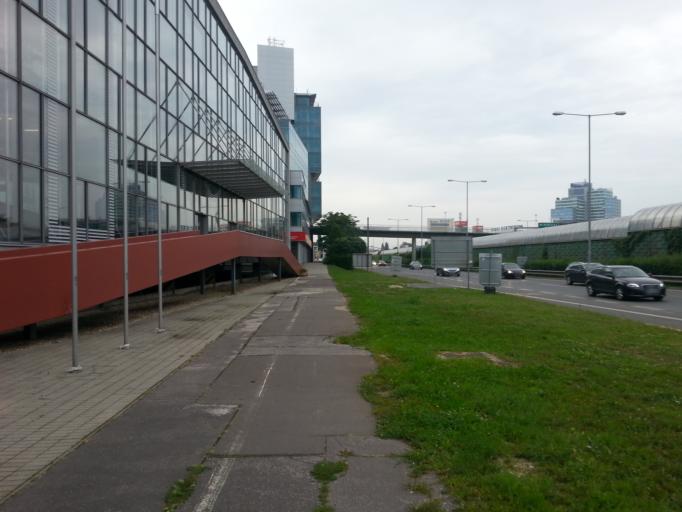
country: SK
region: Bratislavsky
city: Bratislava
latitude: 48.1311
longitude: 17.1141
